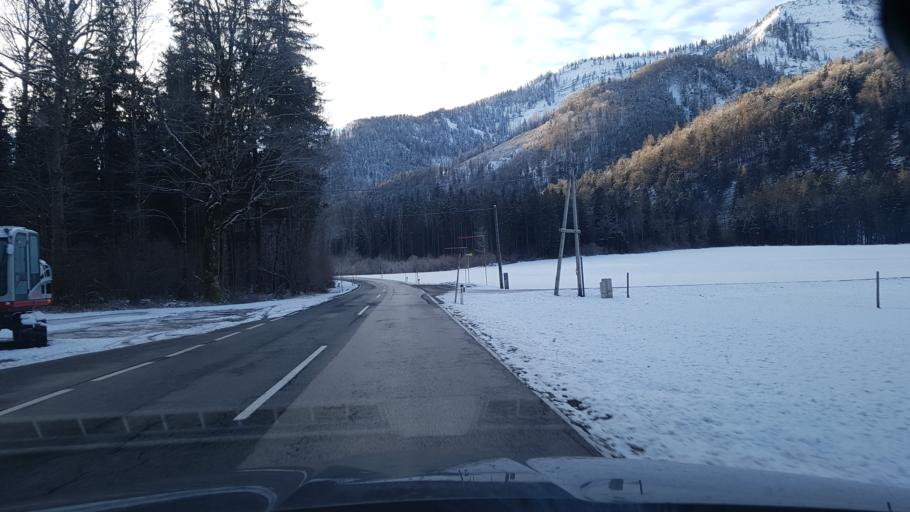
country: AT
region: Salzburg
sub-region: Politischer Bezirk Salzburg-Umgebung
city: Faistenau
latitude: 47.7419
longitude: 13.2573
